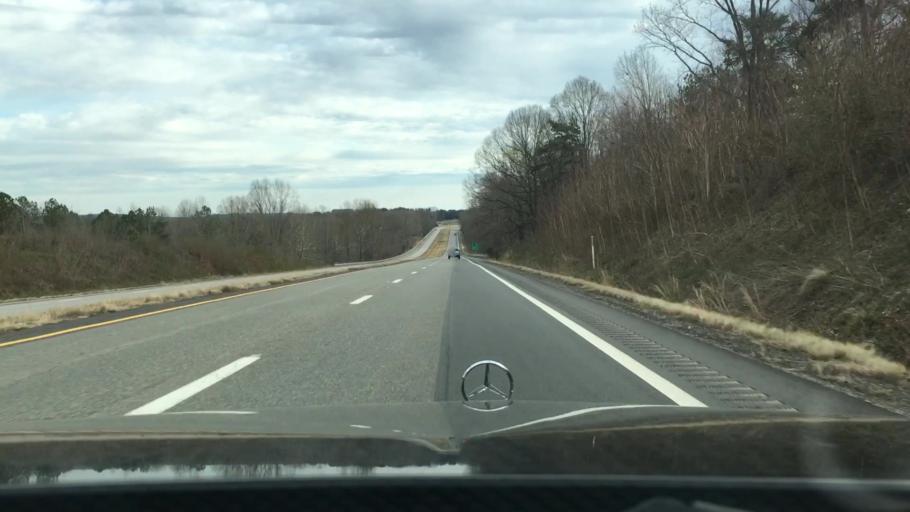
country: US
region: Virginia
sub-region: Pittsylvania County
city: Chatham
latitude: 36.8445
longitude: -79.3905
